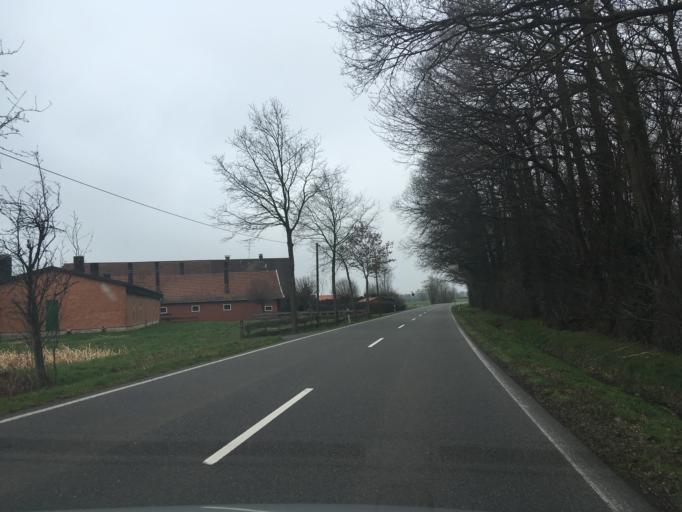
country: DE
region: North Rhine-Westphalia
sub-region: Regierungsbezirk Munster
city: Rhede
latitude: 51.8584
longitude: 6.7494
